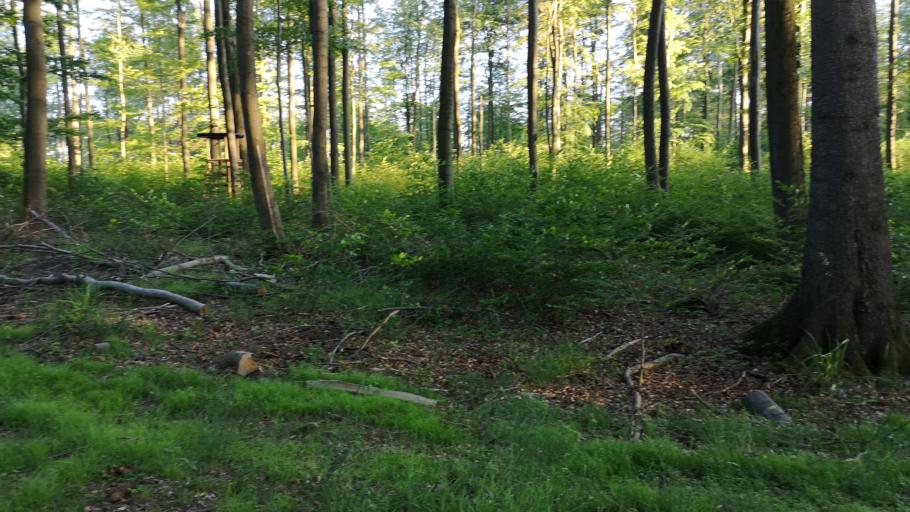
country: DE
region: Saxony-Anhalt
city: Stolberg
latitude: 51.5725
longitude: 10.9747
